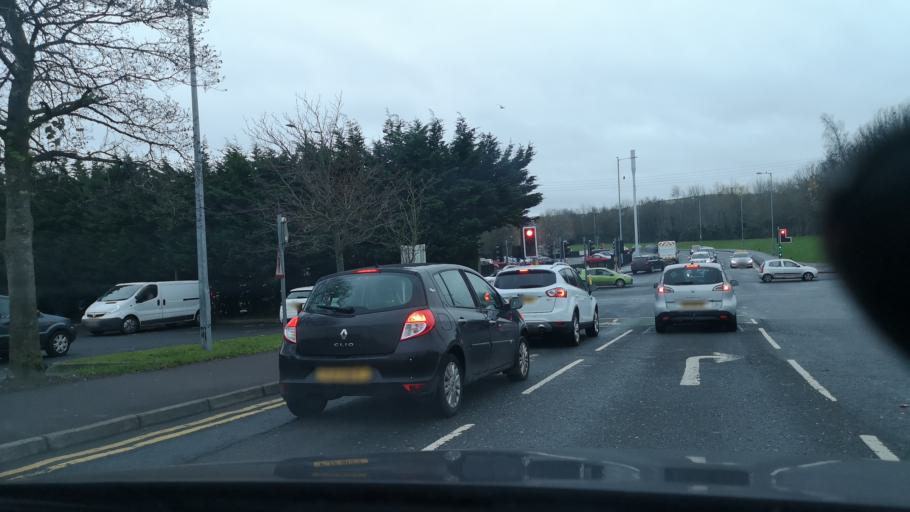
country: GB
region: Northern Ireland
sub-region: Castlereagh District
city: Dundonald
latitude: 54.5954
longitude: -5.8095
